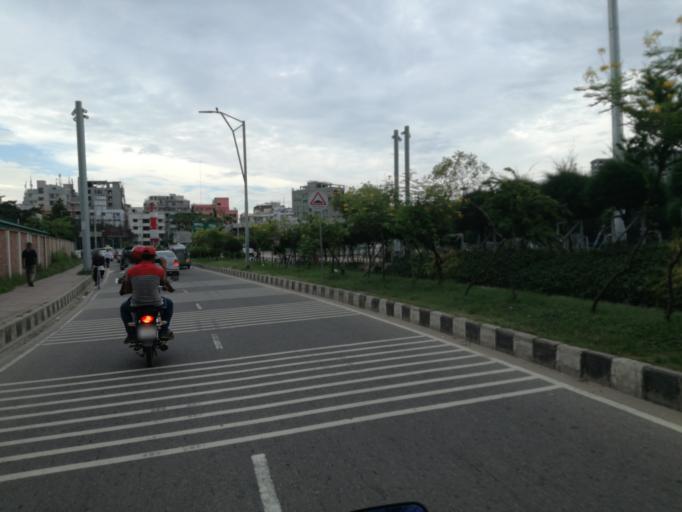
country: BD
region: Dhaka
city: Paltan
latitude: 23.7704
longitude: 90.4127
